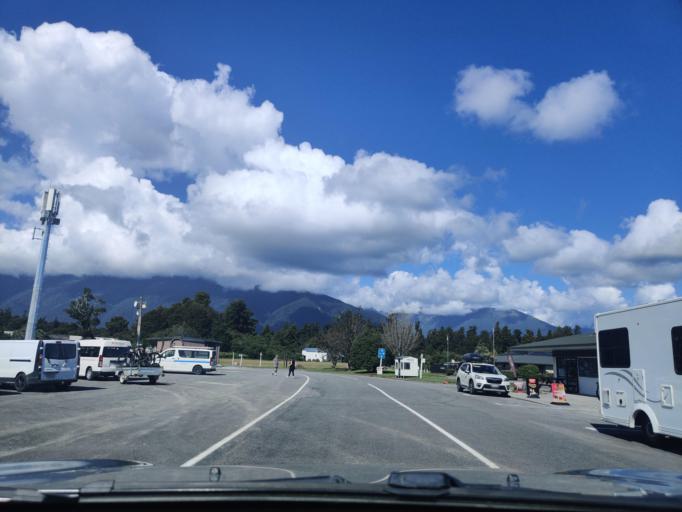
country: NZ
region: Otago
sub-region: Queenstown-Lakes District
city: Wanaka
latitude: -43.8800
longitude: 169.0421
